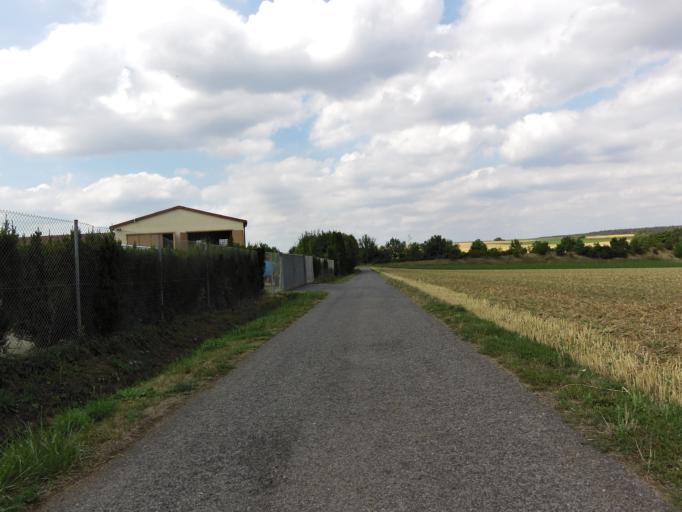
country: DE
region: Bavaria
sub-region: Regierungsbezirk Unterfranken
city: Estenfeld
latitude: 49.8348
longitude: 9.9975
